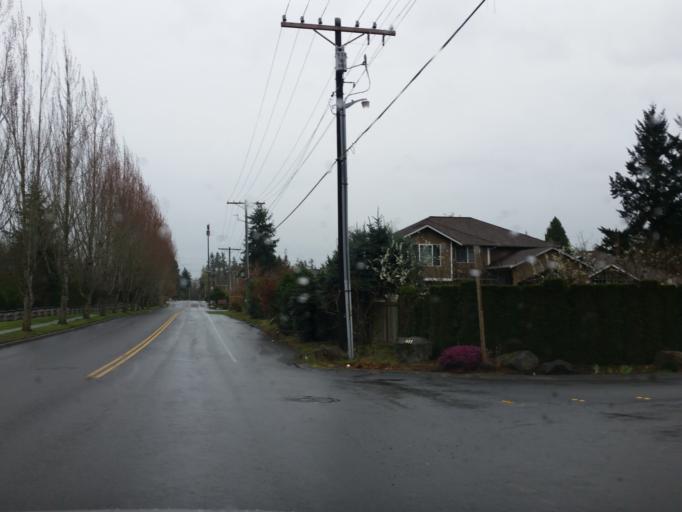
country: US
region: Washington
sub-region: Snohomish County
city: Silver Firs
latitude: 47.8925
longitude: -122.1769
